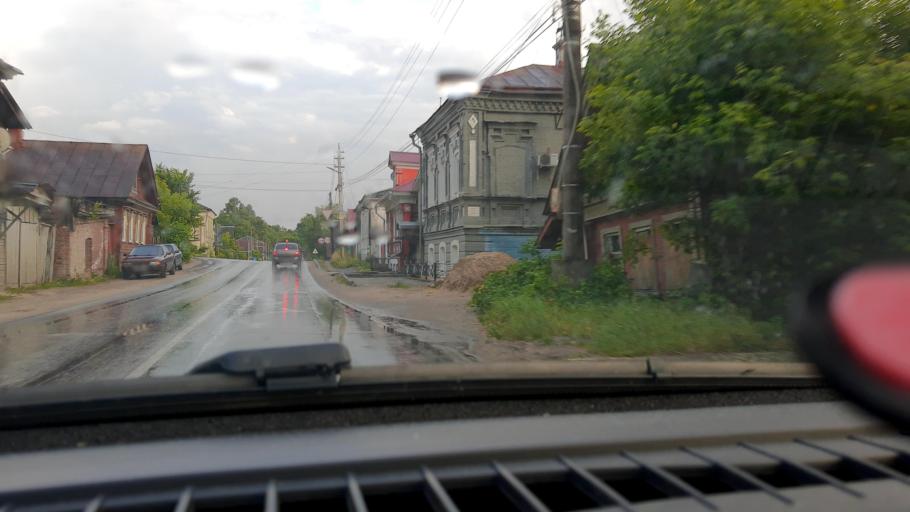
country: RU
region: Nizjnij Novgorod
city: Gorodets
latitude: 56.6532
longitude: 43.4647
